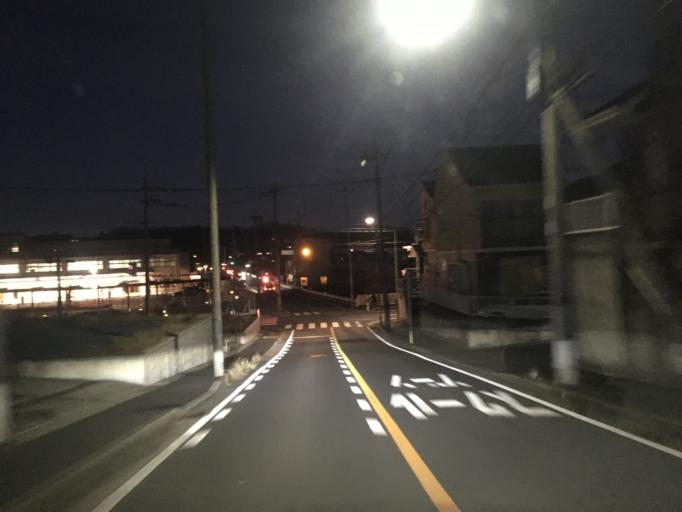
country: JP
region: Tokyo
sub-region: Machida-shi
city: Machida
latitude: 35.5570
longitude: 139.5227
